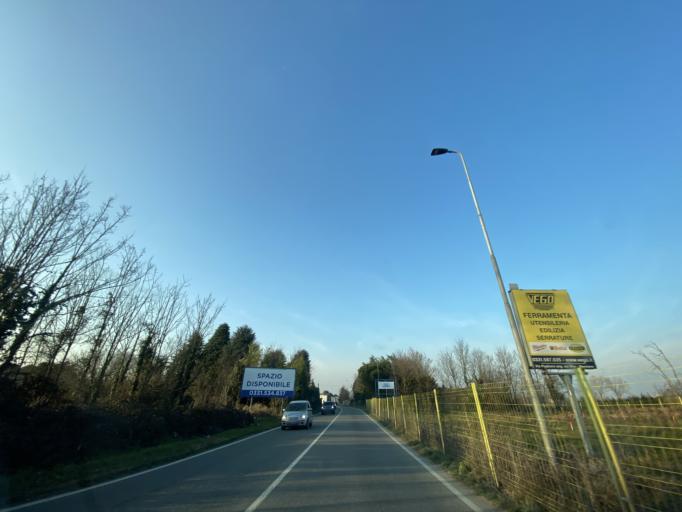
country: IT
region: Lombardy
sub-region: Citta metropolitana di Milano
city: Passirana
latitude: 45.5448
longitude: 9.0327
